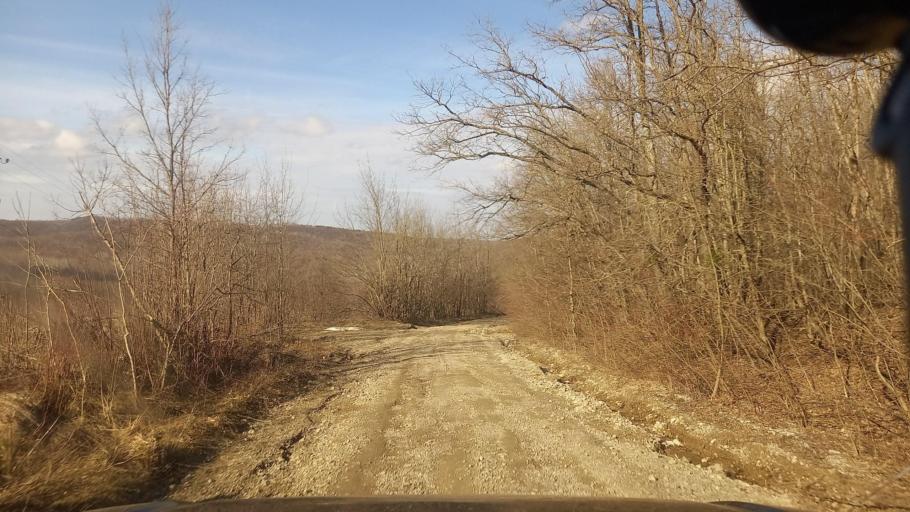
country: RU
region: Krasnodarskiy
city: Goryachiy Klyuch
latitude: 44.6899
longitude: 38.9778
